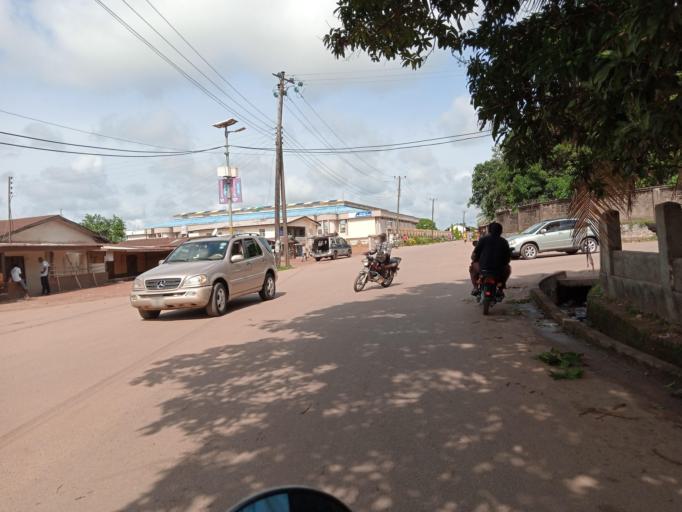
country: SL
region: Southern Province
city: Bo
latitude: 7.9609
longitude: -11.7409
